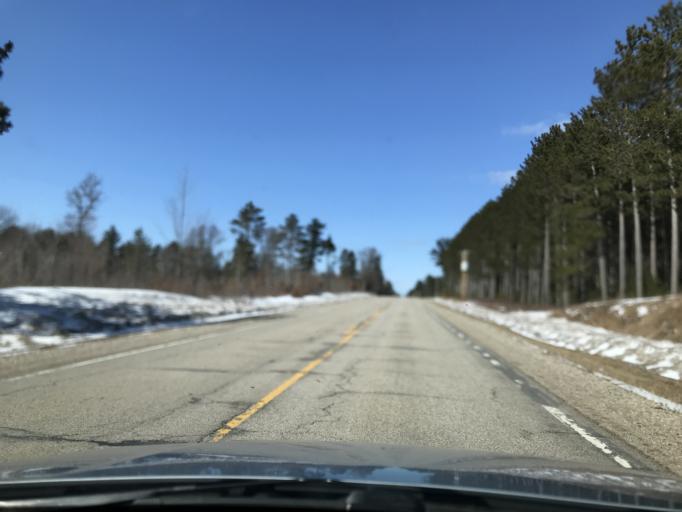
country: US
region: Wisconsin
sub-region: Marinette County
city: Niagara
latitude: 45.3822
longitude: -88.0998
